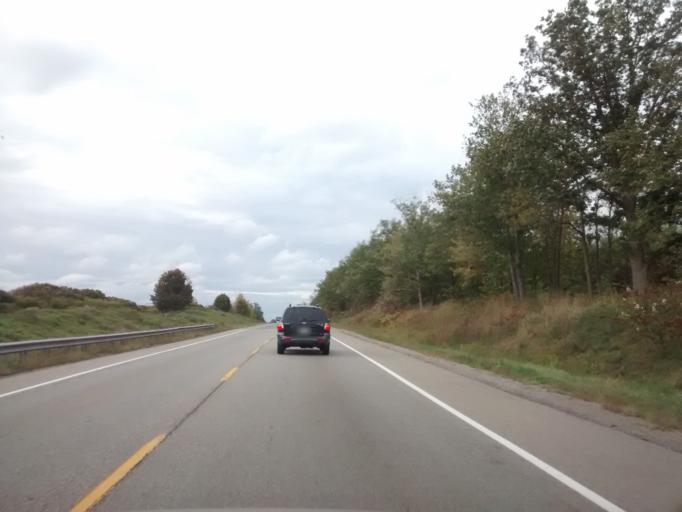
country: CA
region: Ontario
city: Ancaster
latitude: 43.0730
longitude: -79.9747
